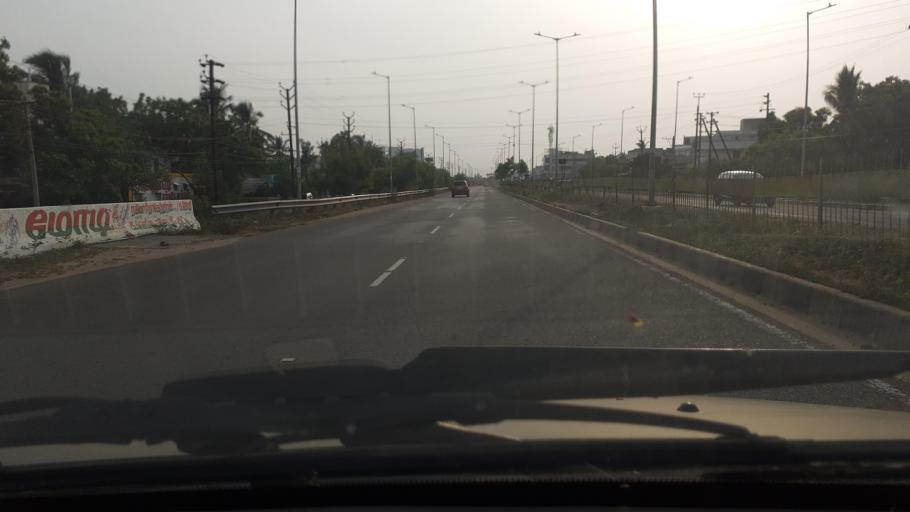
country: IN
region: Tamil Nadu
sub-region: Tirunelveli Kattabo
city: Tirunelveli
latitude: 8.7138
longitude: 77.7770
